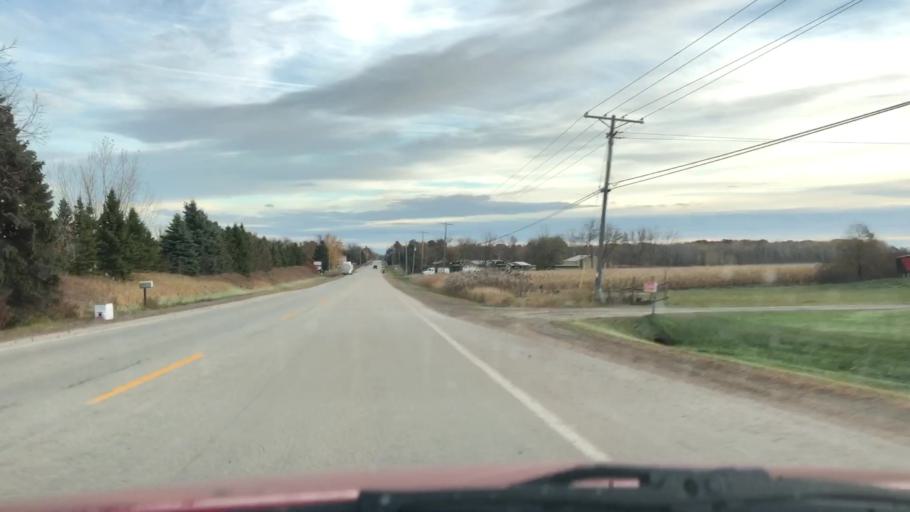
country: US
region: Wisconsin
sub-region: Brown County
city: Oneida
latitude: 44.4356
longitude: -88.2342
